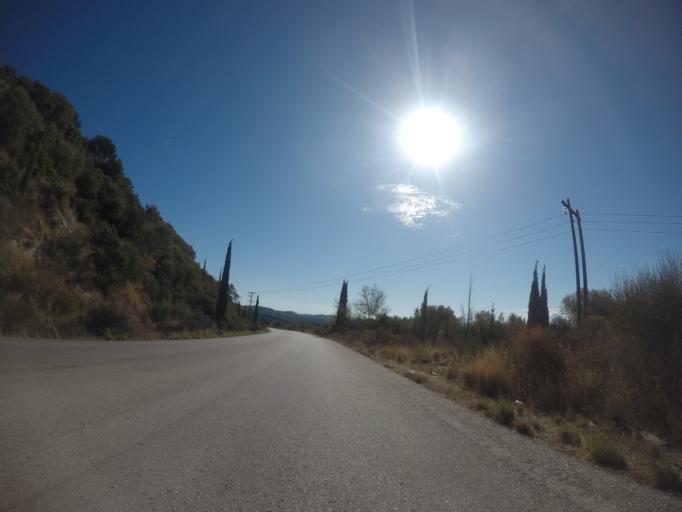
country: GR
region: Epirus
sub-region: Nomos Prevezis
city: Neos Oropos
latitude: 39.1025
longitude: 20.6407
